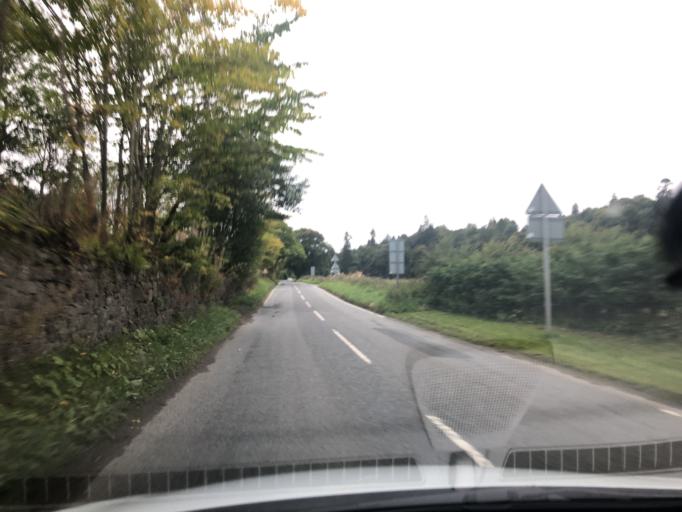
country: GB
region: Scotland
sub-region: Perth and Kinross
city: Pitlochry
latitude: 56.7455
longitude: -3.7824
